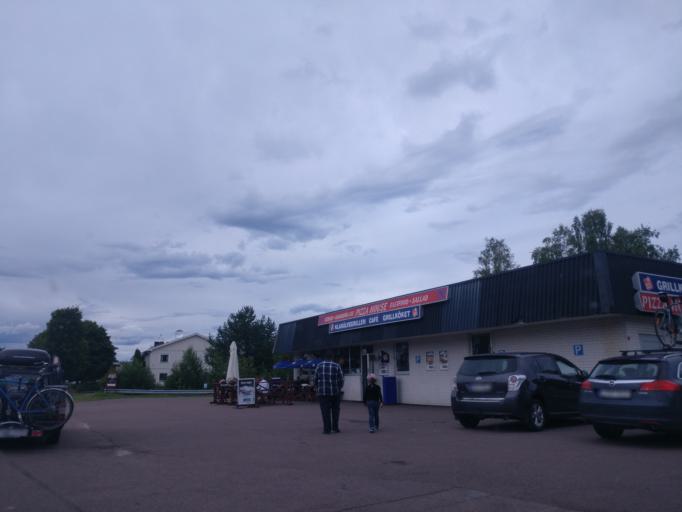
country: SE
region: Vaermland
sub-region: Hagfors Kommun
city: Ekshaerad
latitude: 60.1740
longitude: 13.4962
